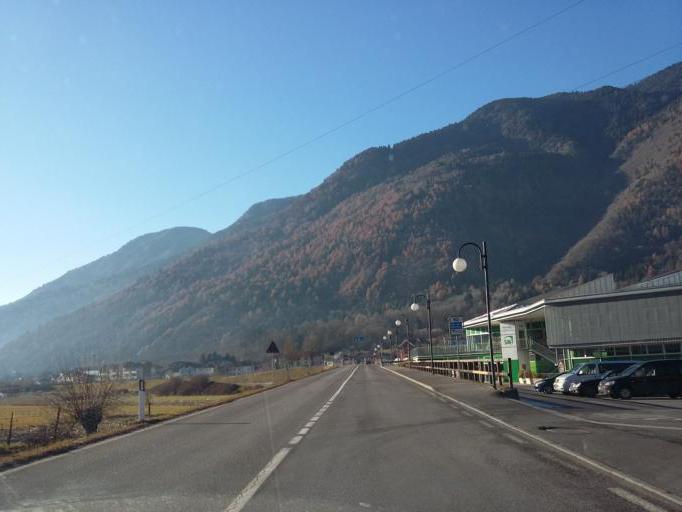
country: IT
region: Trentino-Alto Adige
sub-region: Provincia di Trento
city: Storo
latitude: 45.8545
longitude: 10.5708
